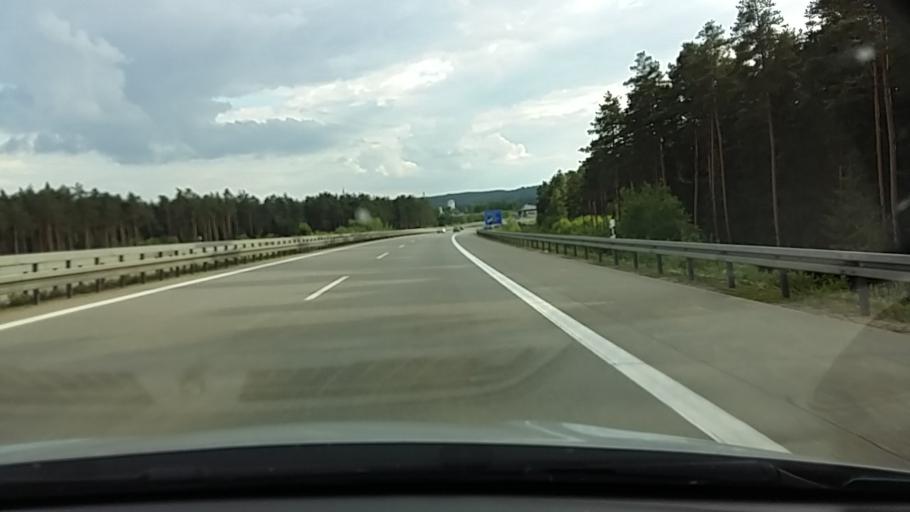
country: DE
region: Bavaria
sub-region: Upper Palatinate
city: Ebermannsdorf
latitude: 49.4052
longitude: 11.9856
